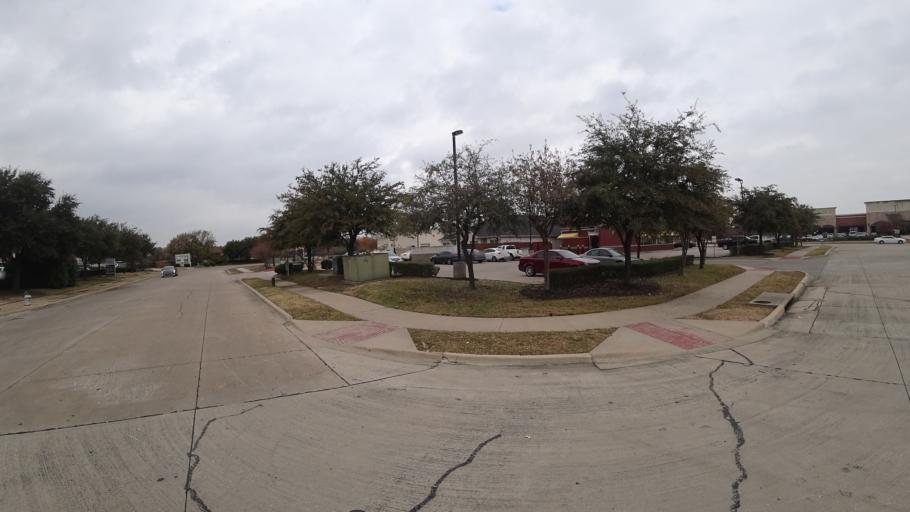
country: US
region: Texas
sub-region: Denton County
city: Lewisville
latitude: 33.0227
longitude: -96.9372
